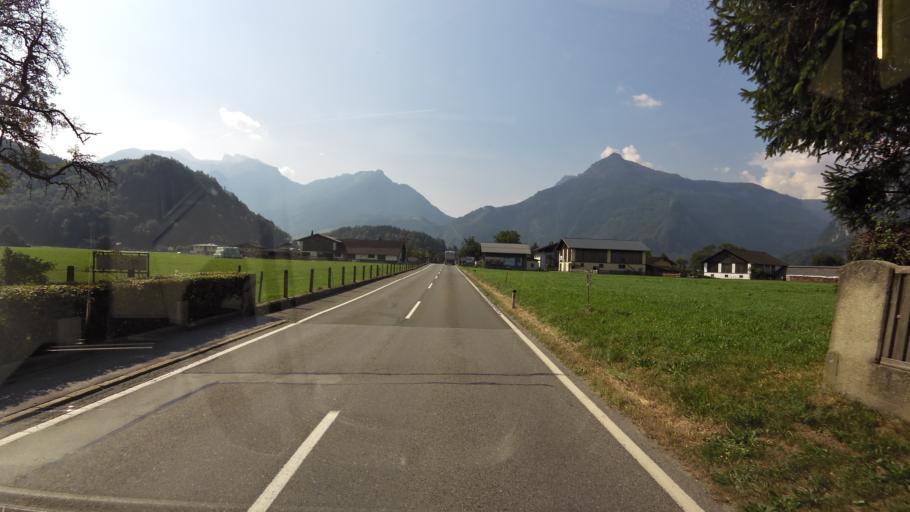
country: AT
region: Salzburg
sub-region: Politischer Bezirk Hallein
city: Golling an der Salzach
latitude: 47.6070
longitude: 13.1678
